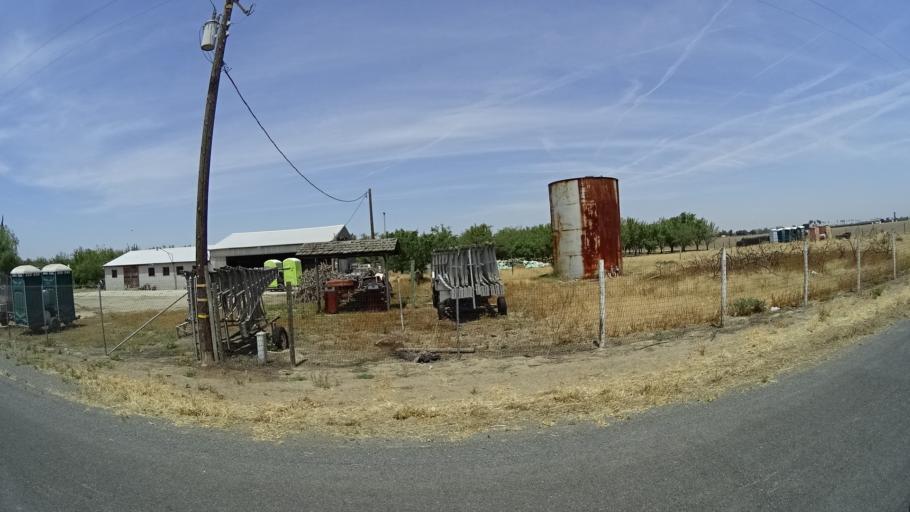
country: US
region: California
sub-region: Fresno County
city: Riverdale
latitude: 36.3948
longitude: -119.8418
